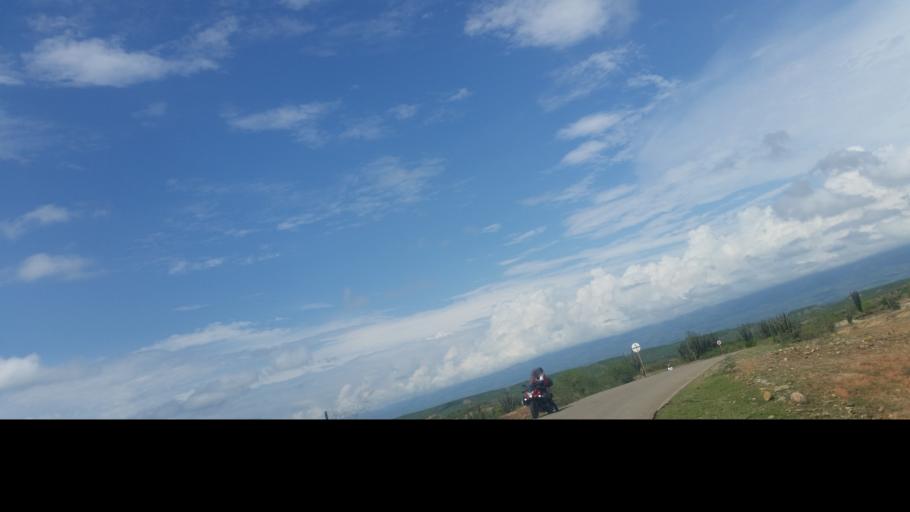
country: CO
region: Huila
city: Villavieja
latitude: 3.2332
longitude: -75.1740
